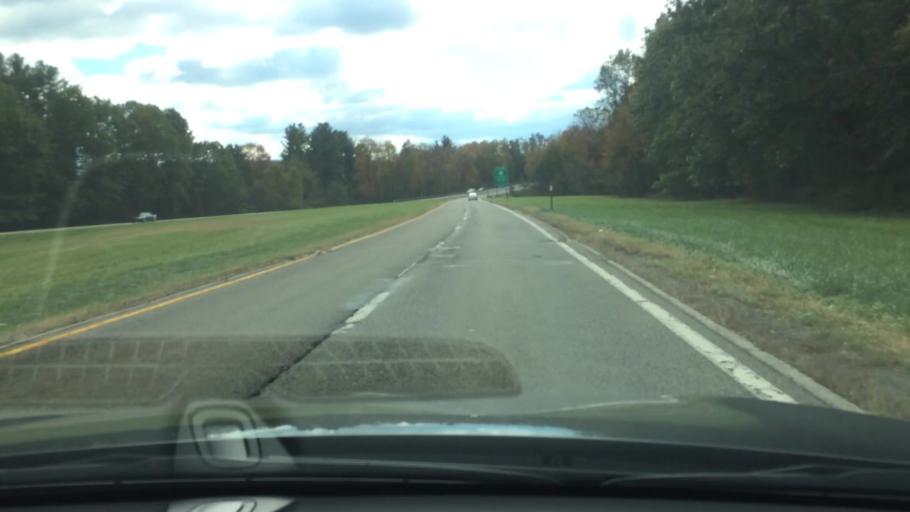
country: US
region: New York
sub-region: Dutchess County
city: Hillside Lake
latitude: 41.5740
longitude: -73.7800
